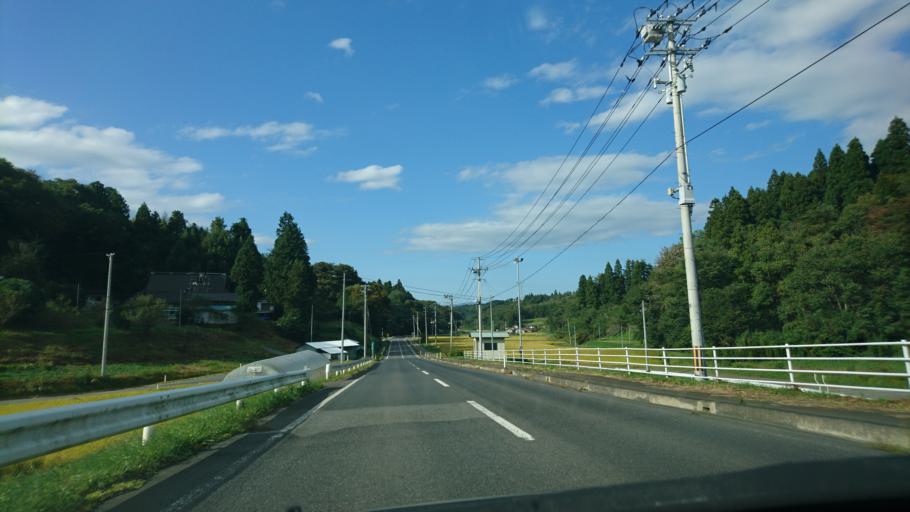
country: JP
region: Iwate
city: Ichinoseki
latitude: 38.8813
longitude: 141.3327
